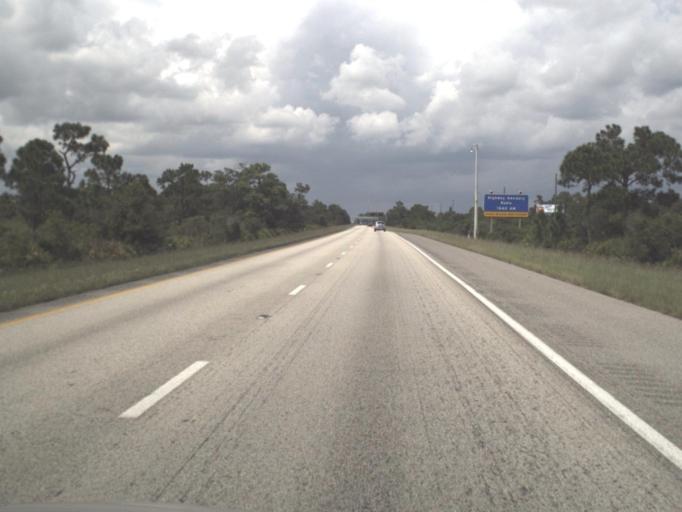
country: US
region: Florida
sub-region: Charlotte County
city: Harbour Heights
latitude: 26.9940
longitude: -82.0318
